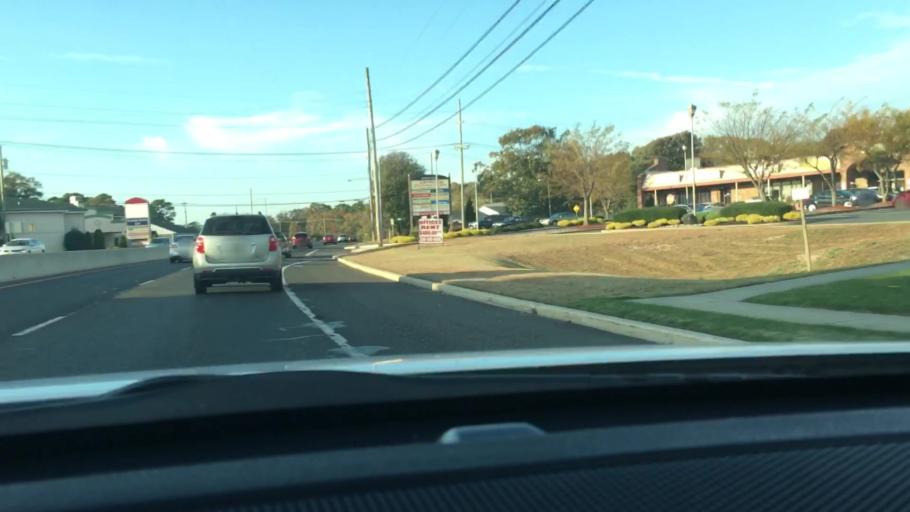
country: US
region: New Jersey
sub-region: Atlantic County
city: Absecon
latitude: 39.4365
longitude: -74.5169
